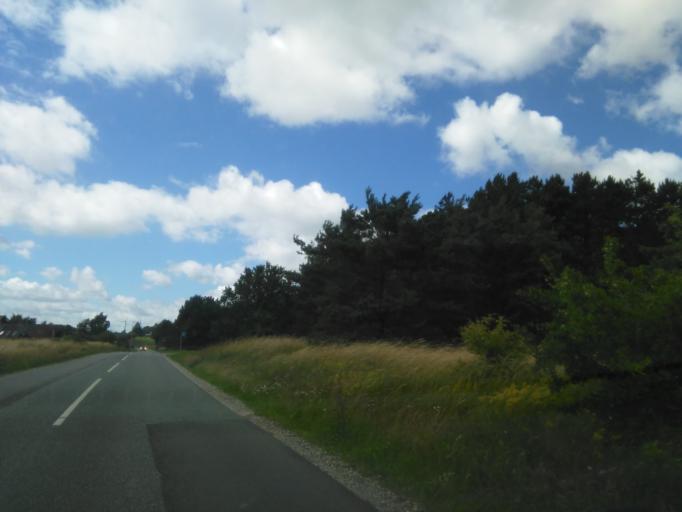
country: DK
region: Central Jutland
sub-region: Syddjurs Kommune
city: Ronde
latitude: 56.2092
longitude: 10.4956
